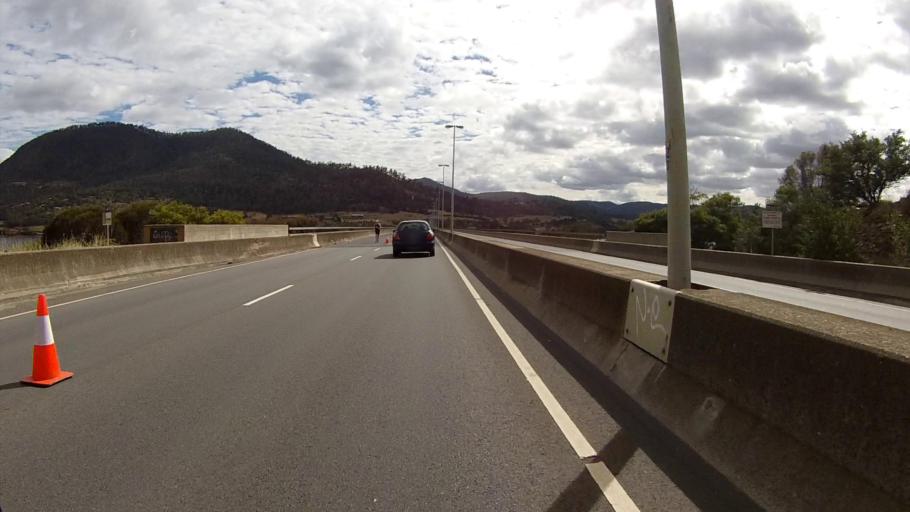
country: AU
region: Tasmania
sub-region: Glenorchy
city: Goodwood
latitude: -42.8211
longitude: 147.3031
